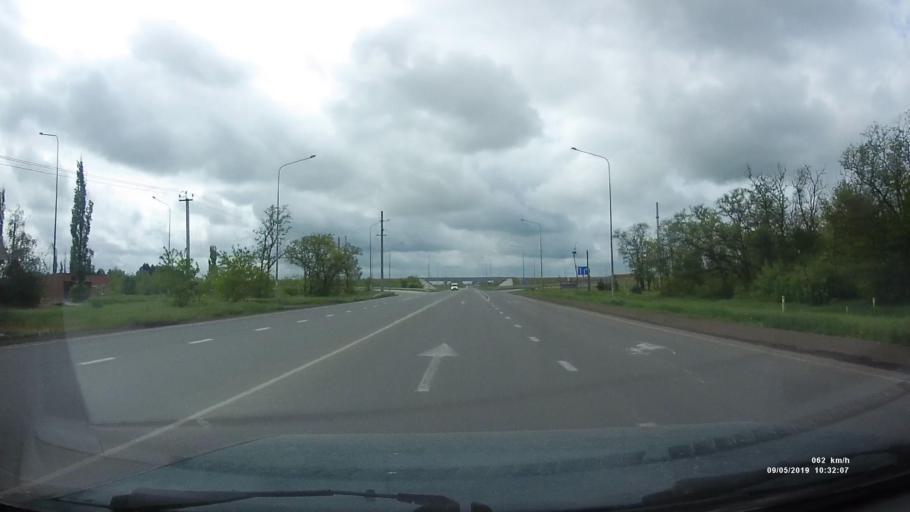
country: RU
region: Rostov
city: Azov
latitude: 47.0754
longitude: 39.4267
